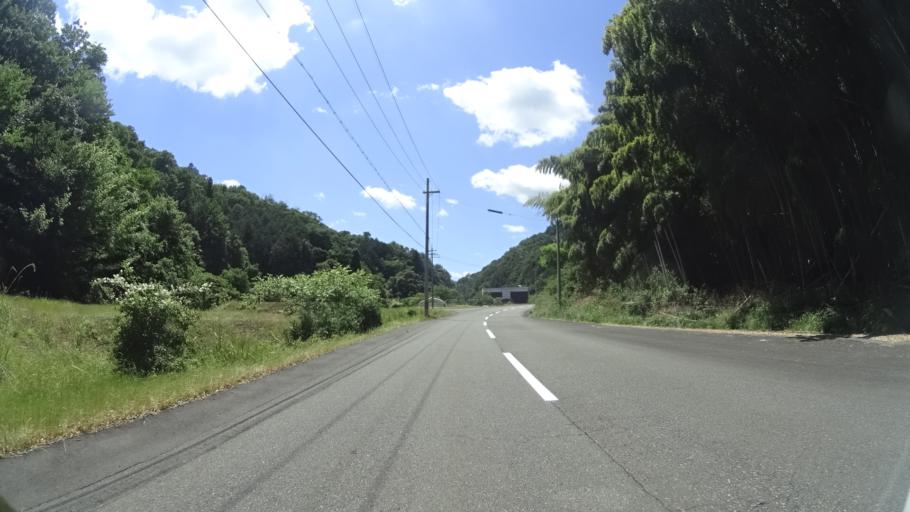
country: JP
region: Kyoto
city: Miyazu
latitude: 35.4195
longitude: 135.1819
